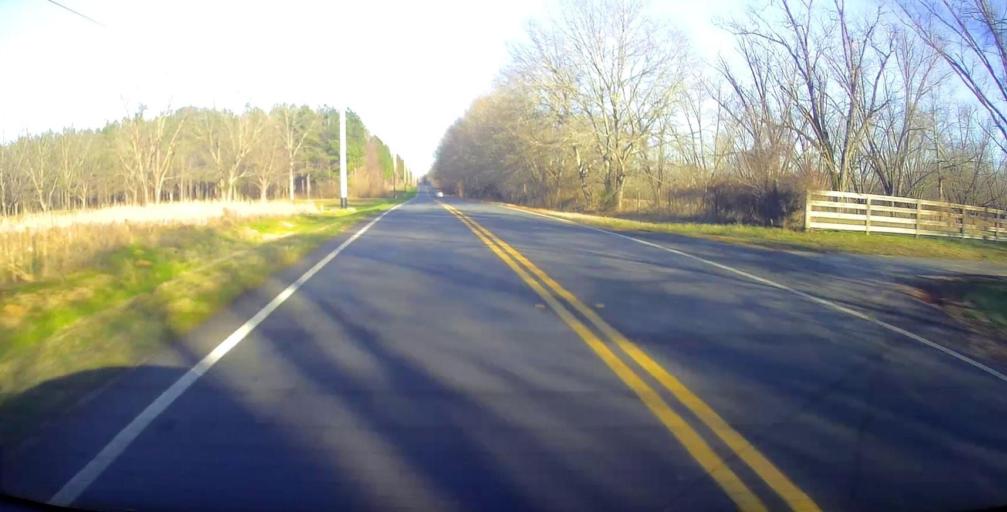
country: US
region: Georgia
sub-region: Harris County
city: Pine Mountain
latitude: 32.9162
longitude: -84.7920
